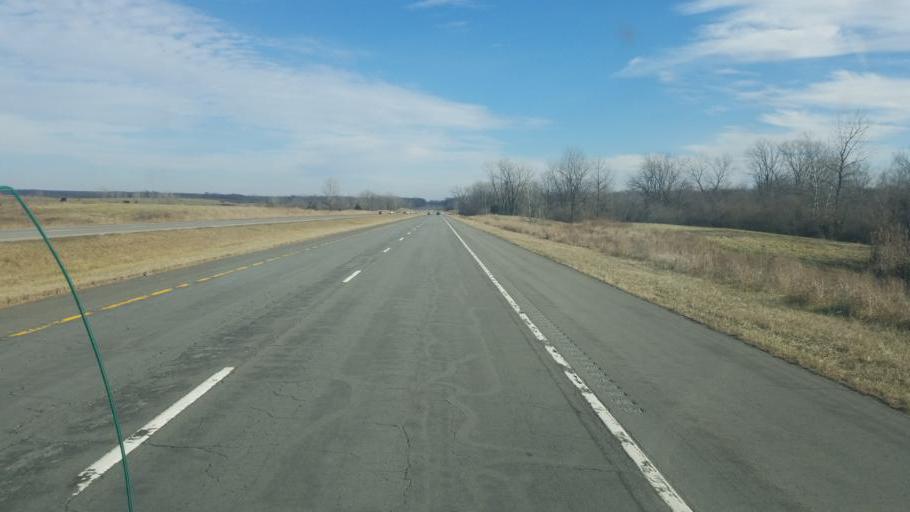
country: US
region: Illinois
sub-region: Saline County
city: Carrier Mills
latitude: 37.7303
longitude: -88.7704
